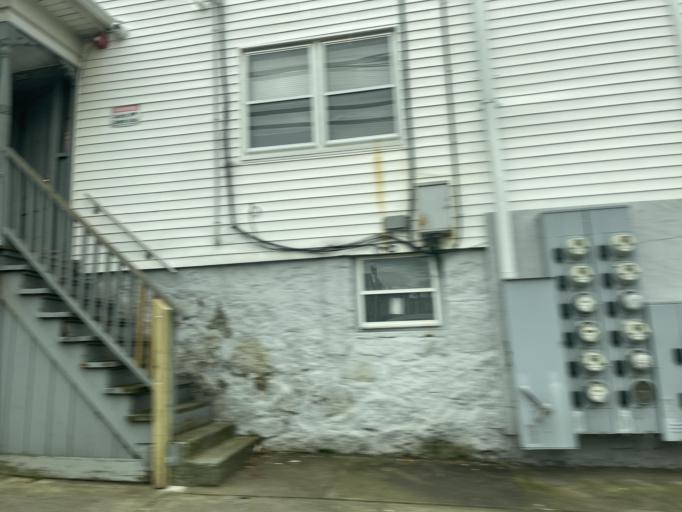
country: US
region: Massachusetts
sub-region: Bristol County
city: Fall River
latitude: 41.6947
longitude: -71.1361
